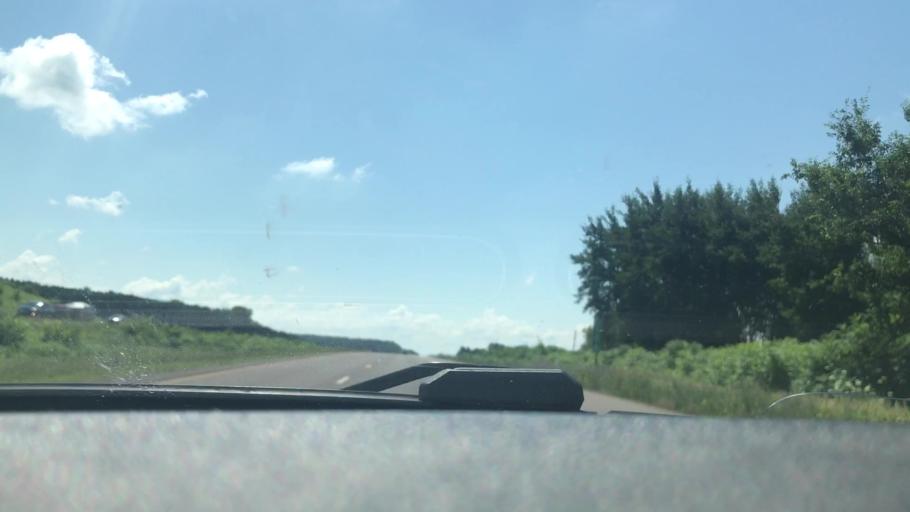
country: US
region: Wisconsin
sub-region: Chippewa County
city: Bloomer
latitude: 45.0440
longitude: -91.4627
